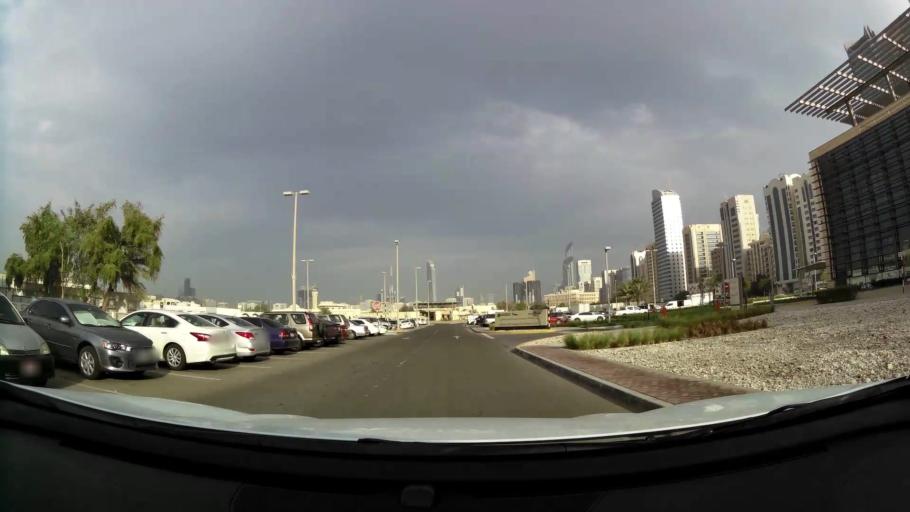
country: AE
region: Abu Dhabi
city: Abu Dhabi
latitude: 24.4694
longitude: 54.3681
